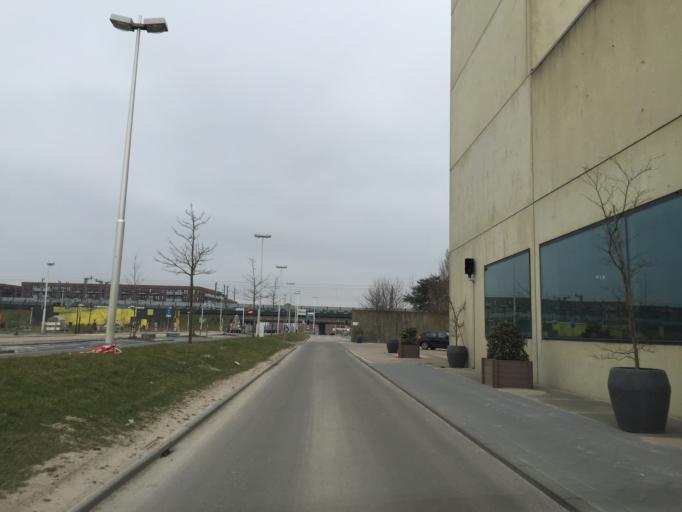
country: NL
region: Utrecht
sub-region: Stichtse Vecht
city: Maarssen
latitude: 52.0980
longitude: 5.0565
